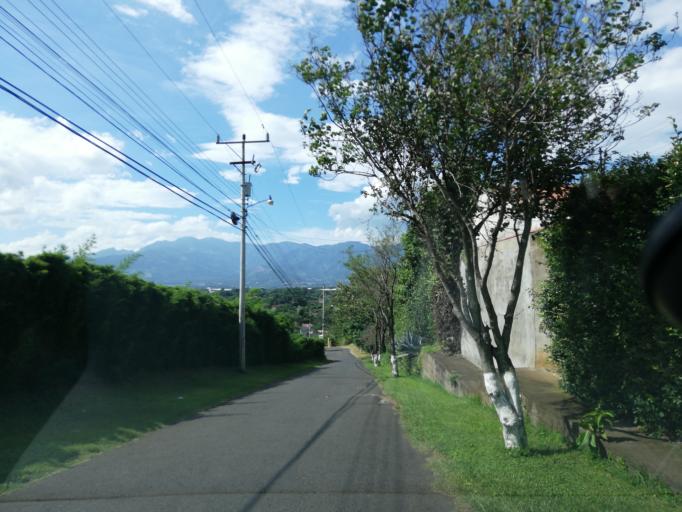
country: CR
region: Alajuela
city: Alajuela
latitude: 9.9837
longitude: -84.2191
